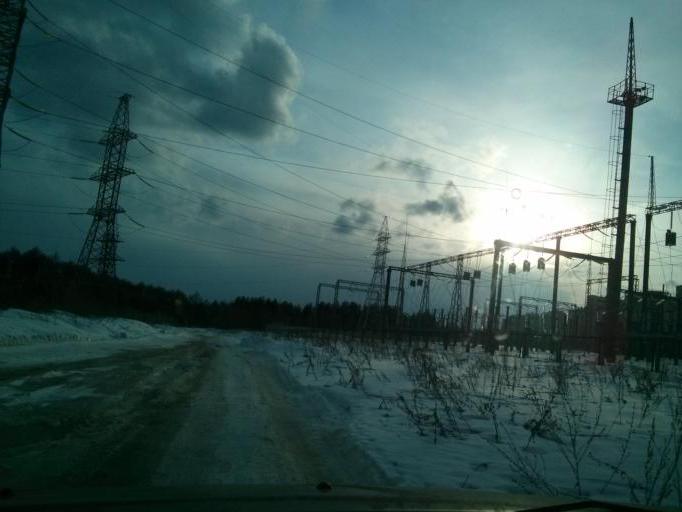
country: RU
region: Nizjnij Novgorod
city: Afonino
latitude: 56.2632
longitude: 44.0298
